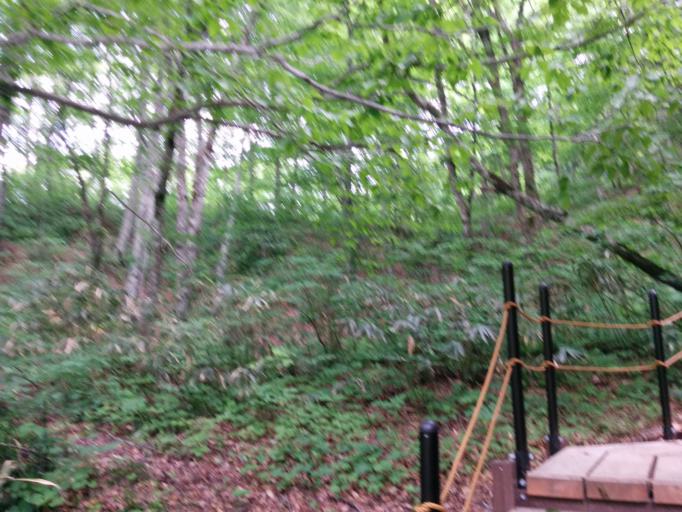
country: JP
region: Aomori
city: Hirosaki
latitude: 40.5221
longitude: 140.1737
